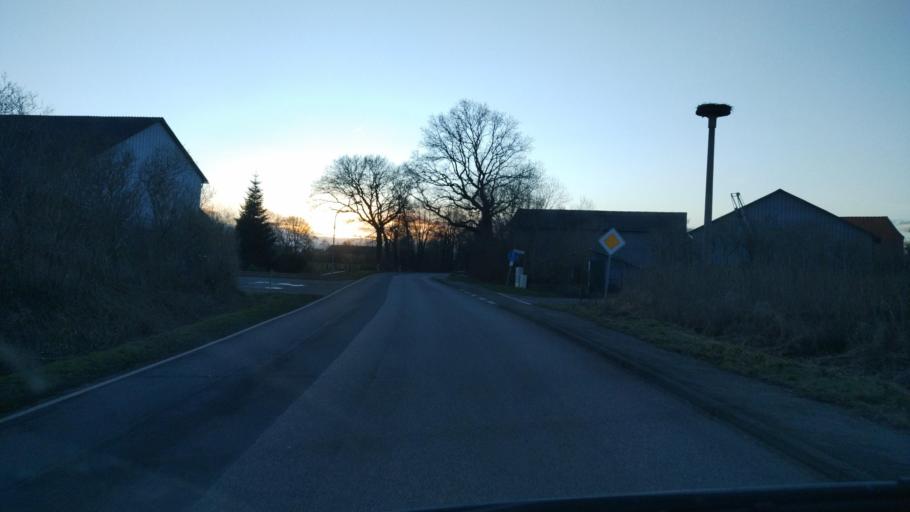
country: DE
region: Schleswig-Holstein
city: Dorpstedt
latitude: 54.4419
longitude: 9.3666
